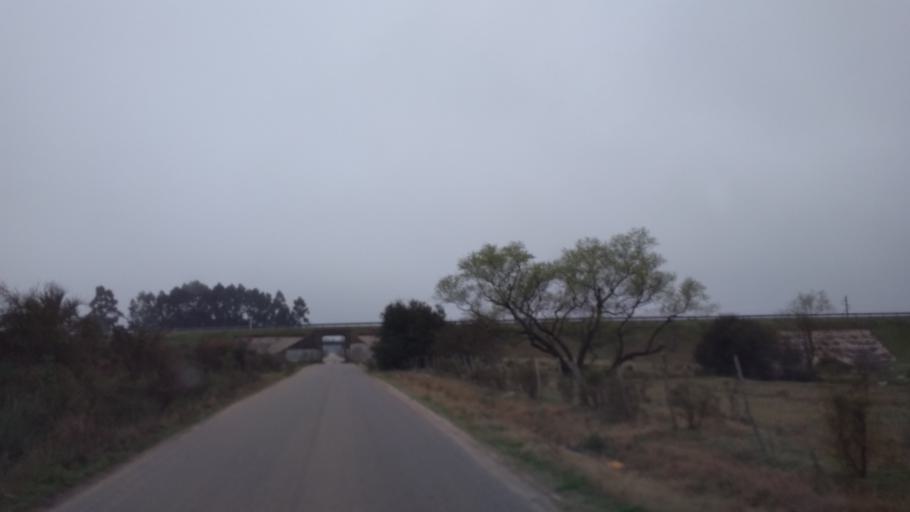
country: UY
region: Florida
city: Florida
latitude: -34.0891
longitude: -56.2084
